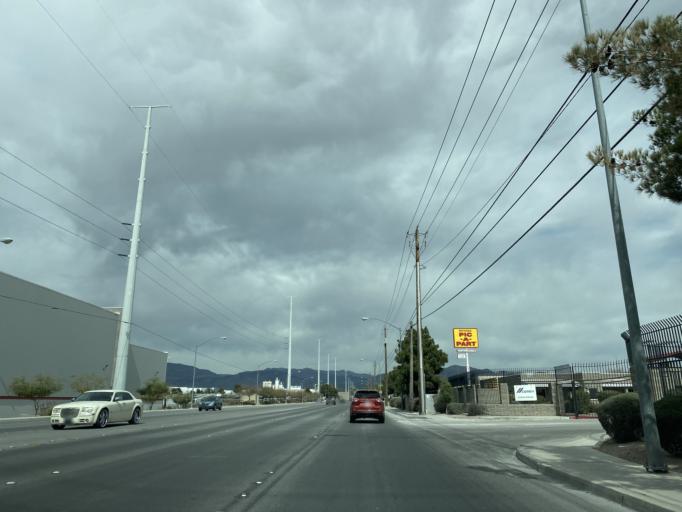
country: US
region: Nevada
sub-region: Clark County
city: Nellis Air Force Base
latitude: 36.2509
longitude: -115.0799
